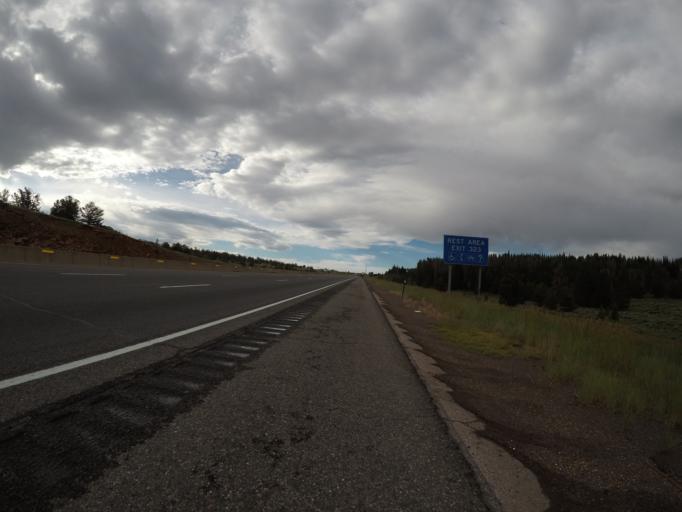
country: US
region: Wyoming
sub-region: Albany County
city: Laramie
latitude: 41.2489
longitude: -105.4435
